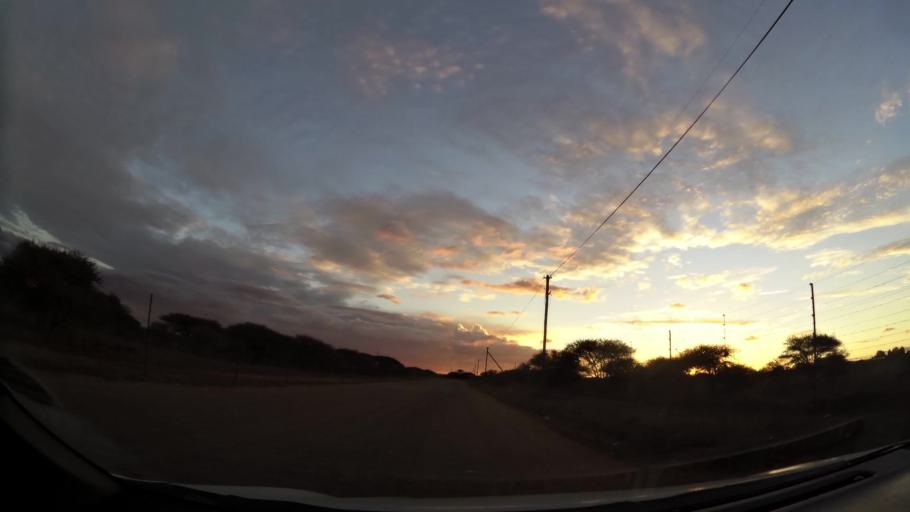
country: ZA
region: Limpopo
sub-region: Capricorn District Municipality
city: Polokwane
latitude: -23.7438
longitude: 29.4645
